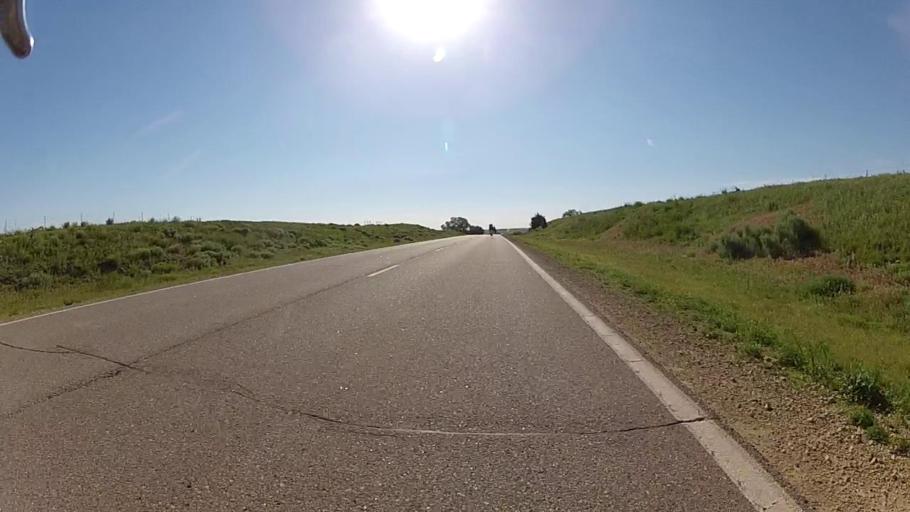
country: US
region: Kansas
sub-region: Barber County
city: Medicine Lodge
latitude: 37.2816
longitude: -98.8895
